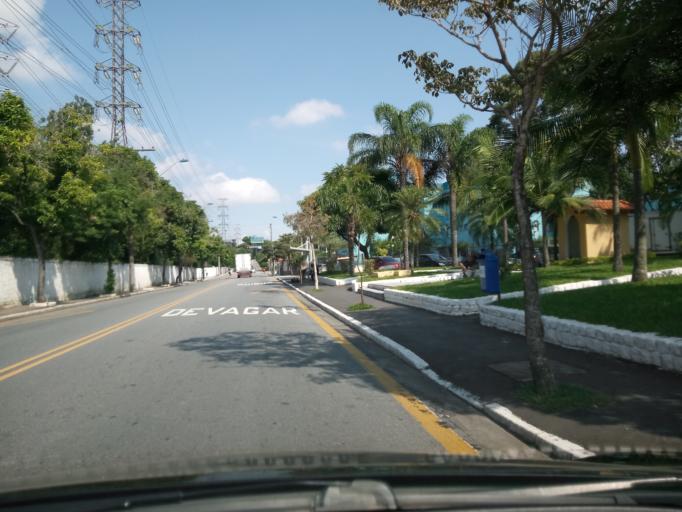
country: BR
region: Sao Paulo
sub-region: Sao Caetano Do Sul
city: Sao Caetano do Sul
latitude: -23.6359
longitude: -46.5754
